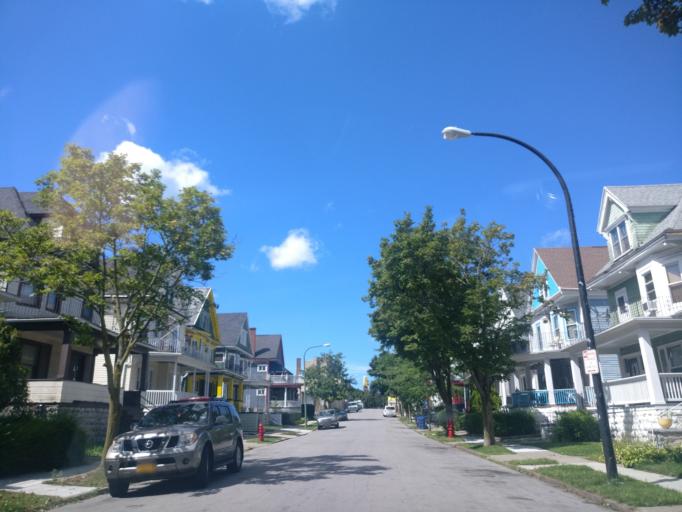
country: US
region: New York
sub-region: Erie County
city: Buffalo
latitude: 42.9103
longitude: -78.8638
